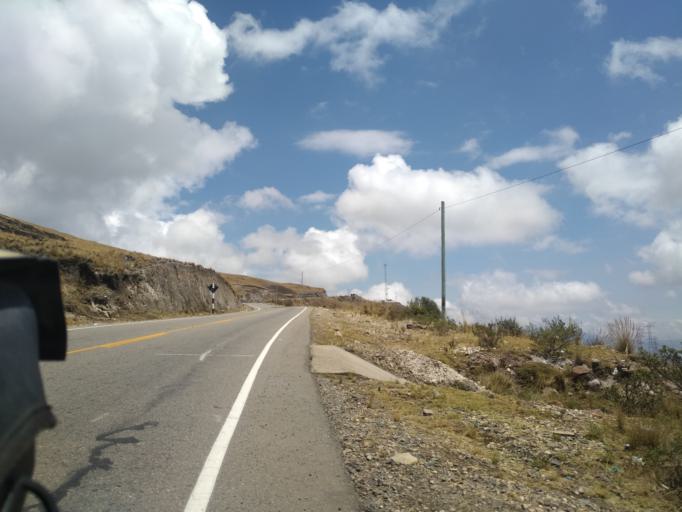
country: PE
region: La Libertad
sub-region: Provincia de Santiago de Chuco
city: Quiruvilca
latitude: -7.9211
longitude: -78.1558
